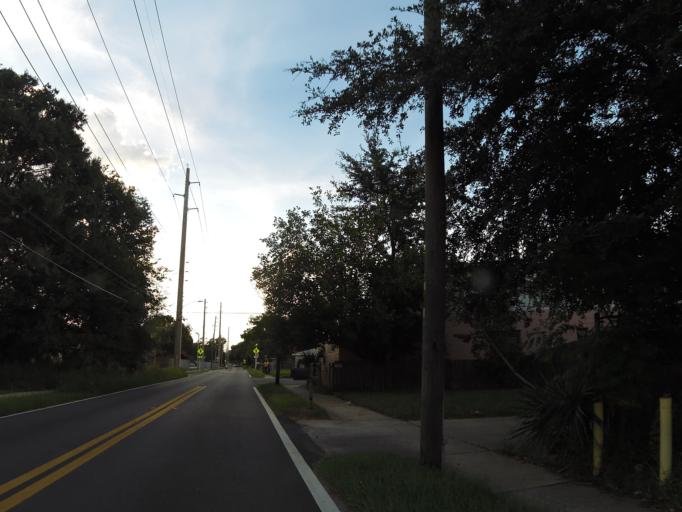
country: US
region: Florida
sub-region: Duval County
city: Jacksonville
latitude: 30.3368
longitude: -81.6844
